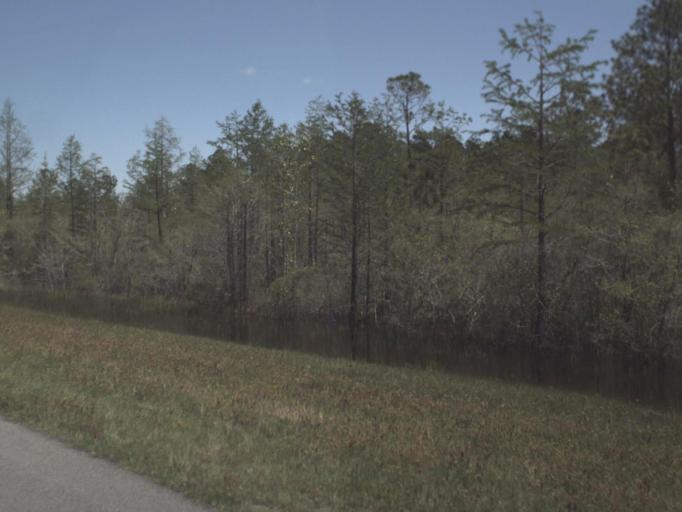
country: US
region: Florida
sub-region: Escambia County
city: Myrtle Grove
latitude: 30.3821
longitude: -87.3503
